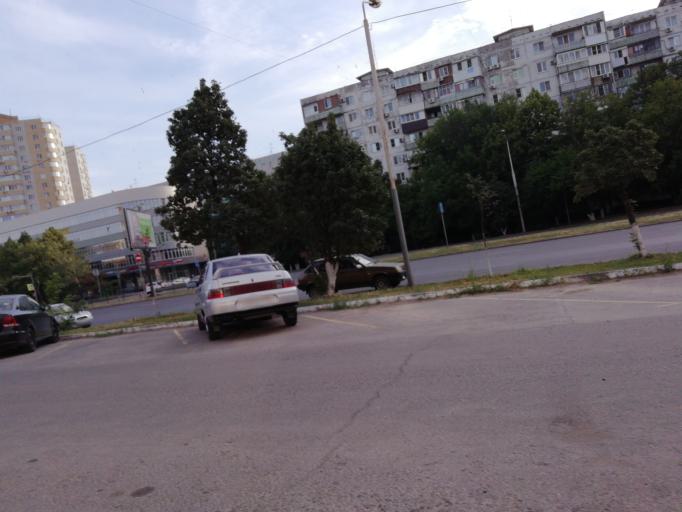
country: RU
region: Rostov
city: Severnyy
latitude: 47.2978
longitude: 39.7132
